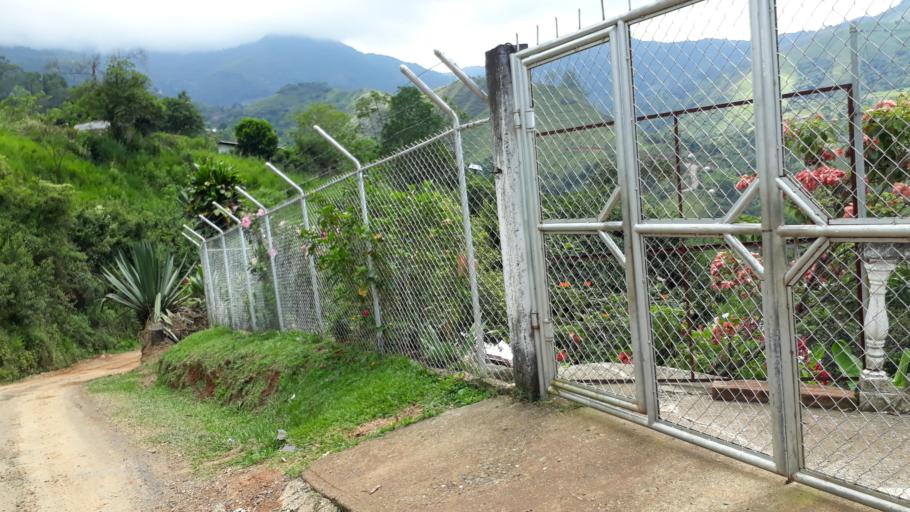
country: CO
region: Valle del Cauca
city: Jamundi
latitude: 3.2701
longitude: -76.6182
